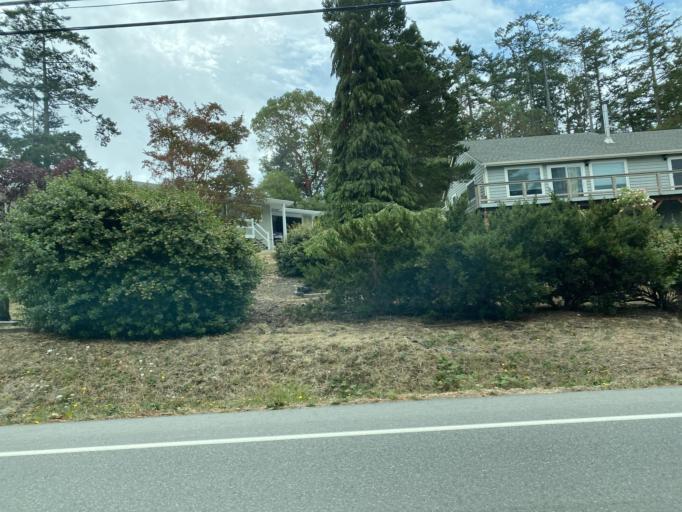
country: US
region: Washington
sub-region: Island County
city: Coupeville
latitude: 48.2139
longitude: -122.7182
